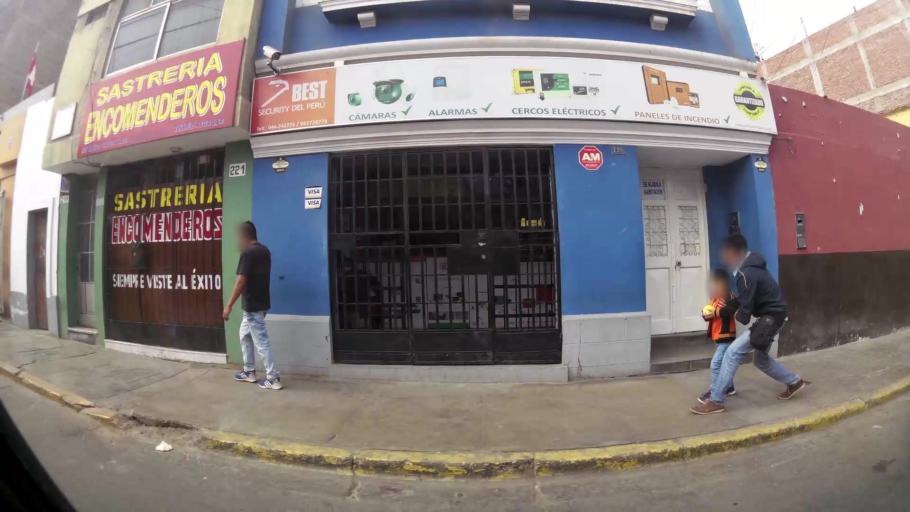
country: PE
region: La Libertad
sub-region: Provincia de Trujillo
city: Trujillo
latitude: -8.1153
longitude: -79.0242
